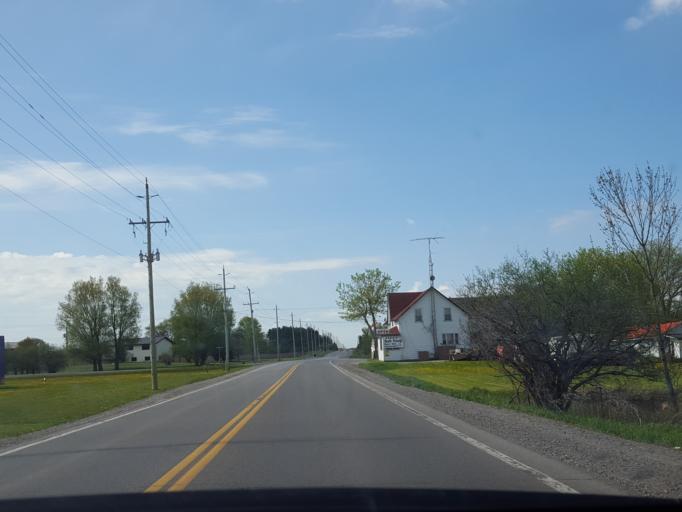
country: CA
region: Ontario
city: Uxbridge
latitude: 44.1716
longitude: -78.8942
